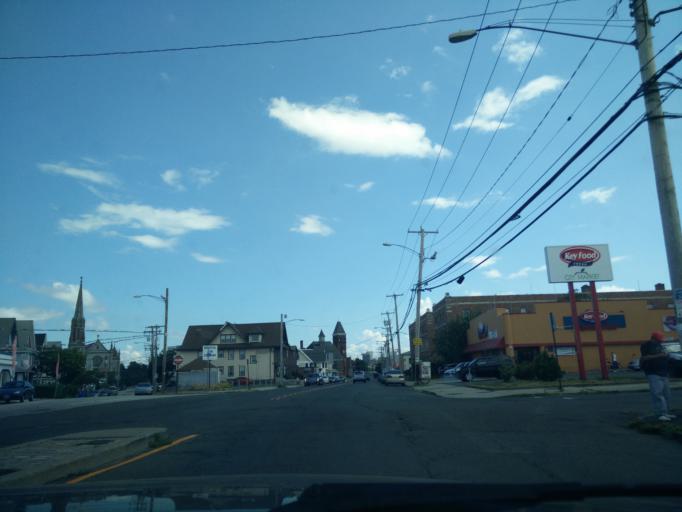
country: US
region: Connecticut
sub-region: Fairfield County
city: Bridgeport
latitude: 41.1942
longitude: -73.1987
